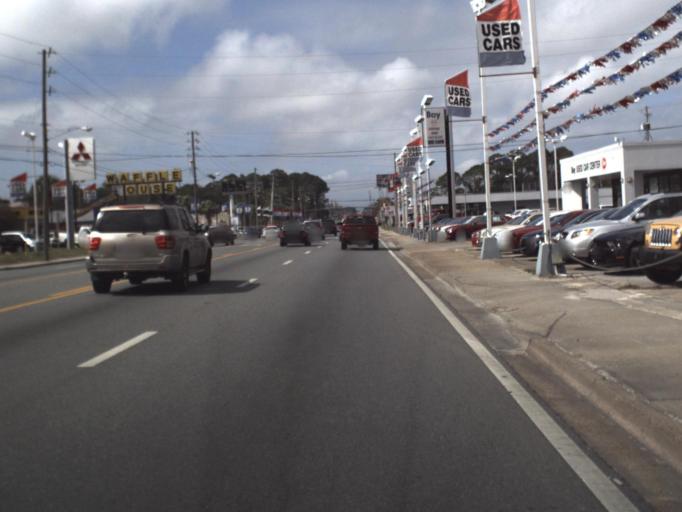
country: US
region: Florida
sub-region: Bay County
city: Panama City
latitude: 30.1753
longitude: -85.6661
